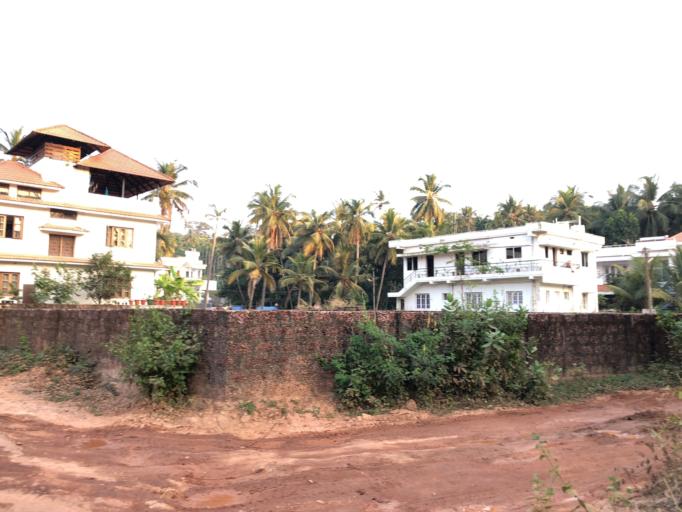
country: IN
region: Karnataka
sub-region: Dakshina Kannada
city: Mangalore
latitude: 12.8776
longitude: 74.8749
